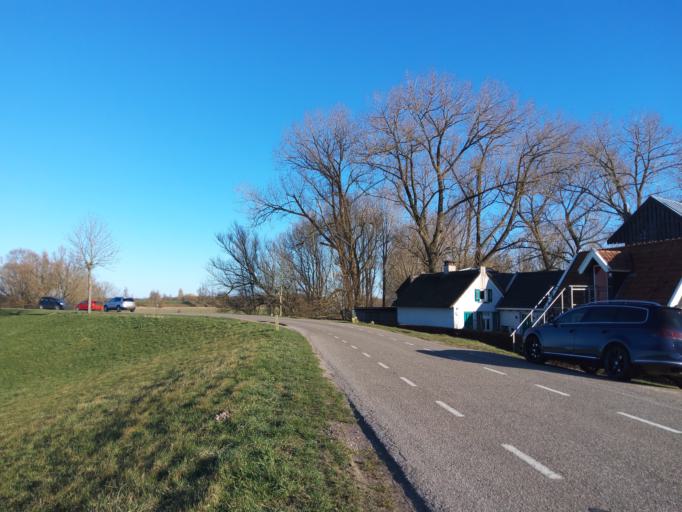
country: NL
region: Gelderland
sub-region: Gemeente Neerijnen
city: Neerijnen
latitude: 51.8282
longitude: 5.3168
